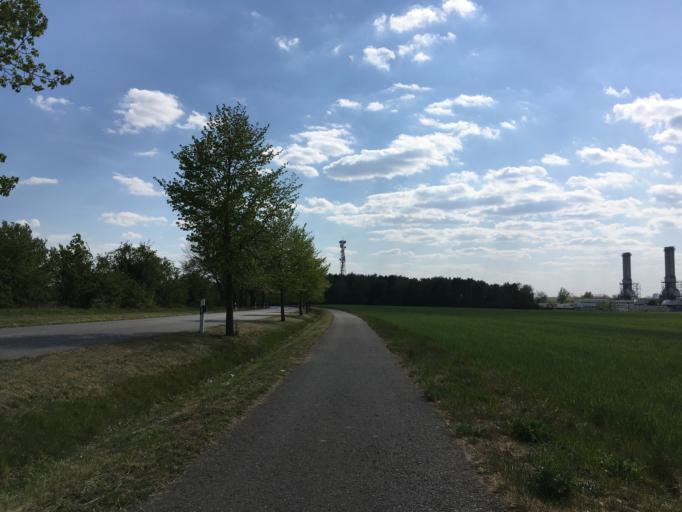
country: DE
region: Brandenburg
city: Ahrensfelde
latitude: 52.5934
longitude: 13.5656
